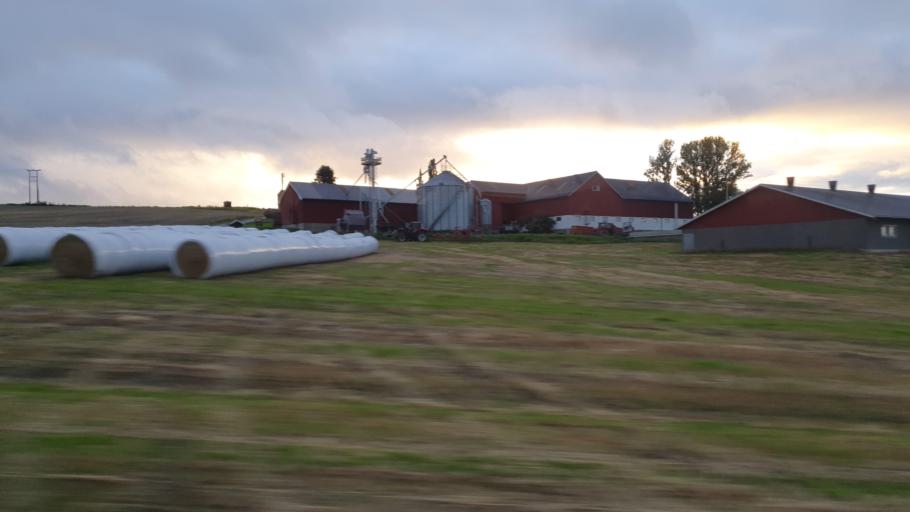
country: NO
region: Nord-Trondelag
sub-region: Levanger
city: Skogn
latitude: 63.6842
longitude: 11.1765
